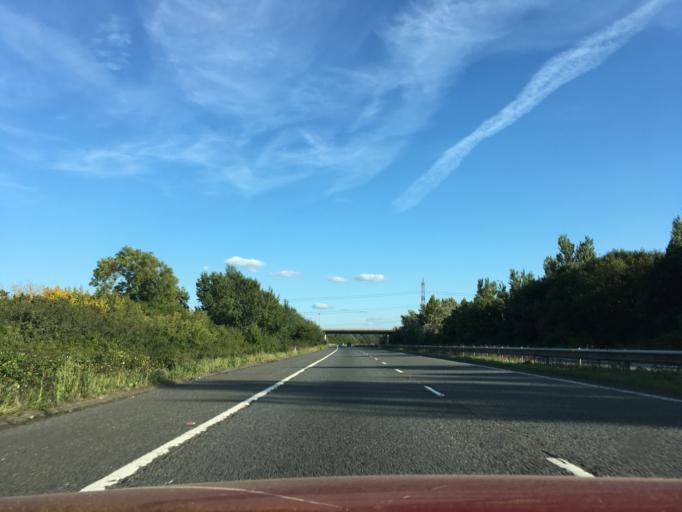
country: GB
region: England
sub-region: South Gloucestershire
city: Severn Beach
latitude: 51.5534
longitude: -2.6454
